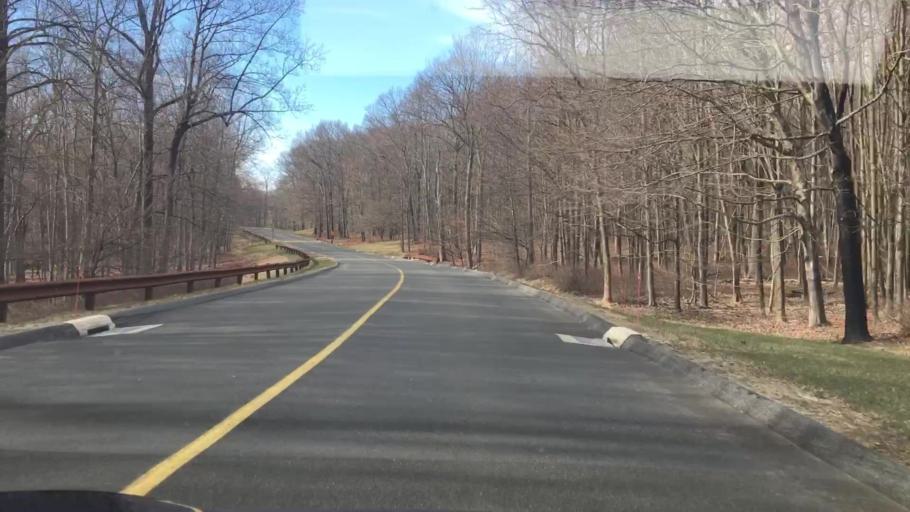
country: US
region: New York
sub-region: Putnam County
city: Peach Lake
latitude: 41.3748
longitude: -73.5178
